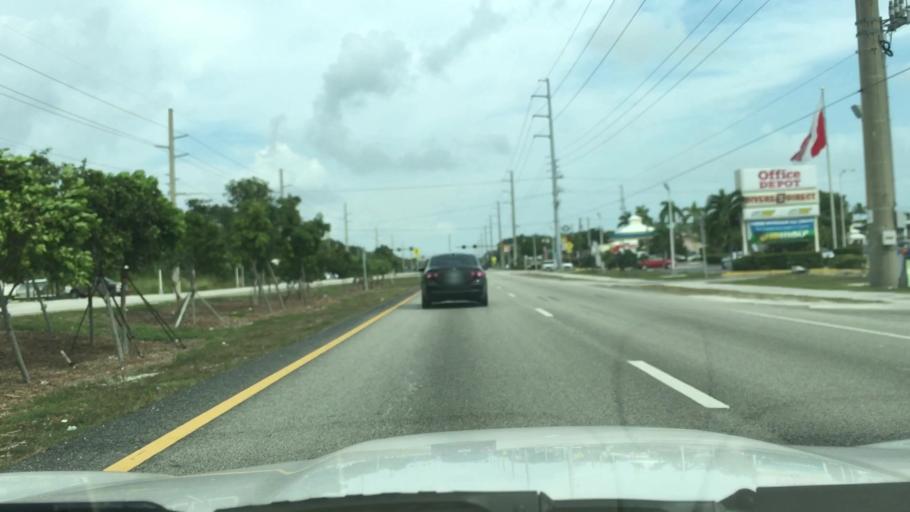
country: US
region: Florida
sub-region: Monroe County
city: Key Largo
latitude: 25.0946
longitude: -80.4404
